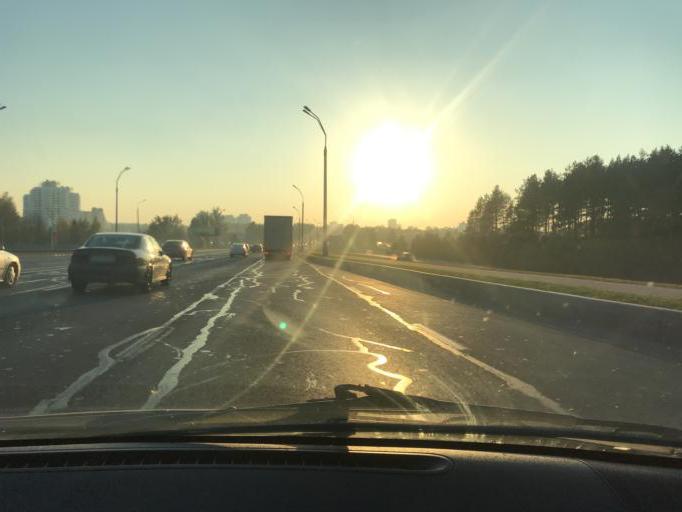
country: BY
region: Minsk
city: Lyeskawka
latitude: 53.9576
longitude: 27.7247
